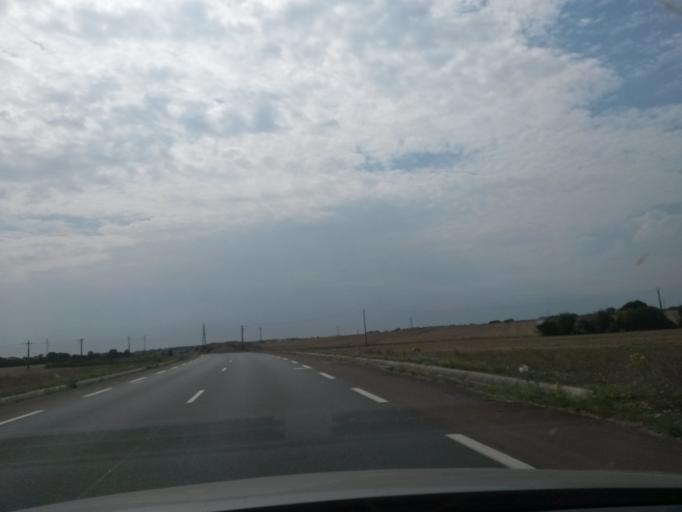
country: FR
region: Poitou-Charentes
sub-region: Departement de la Charente-Maritime
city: Saint-Xandre
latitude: 46.2128
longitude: -1.0909
